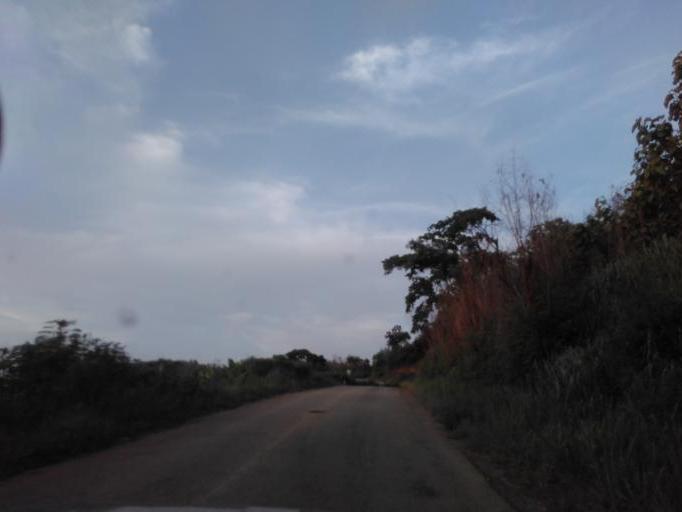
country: GH
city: Bekwai
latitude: 6.5515
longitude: -1.4329
